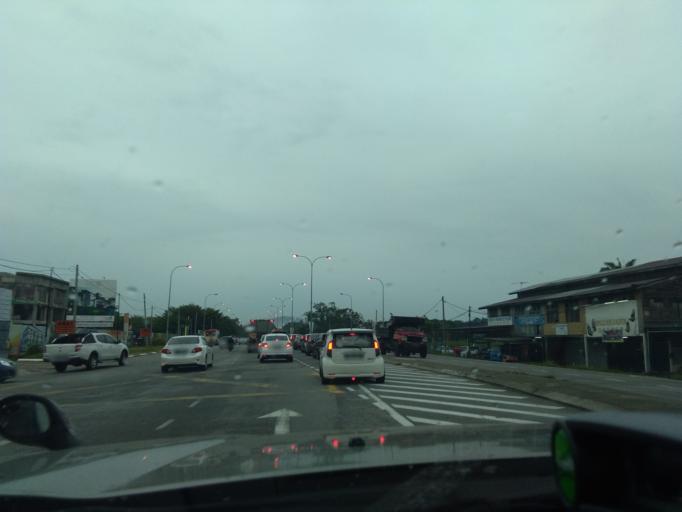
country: MY
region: Penang
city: Nibong Tebal
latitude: 5.1837
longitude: 100.4857
